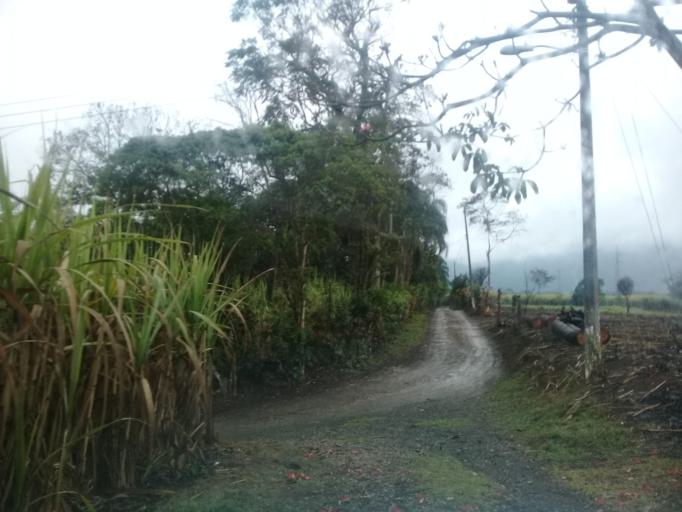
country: MX
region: Veracruz
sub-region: Amatlan de los Reyes
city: Centro de Readaptacion Social
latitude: 18.8208
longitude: -96.9452
